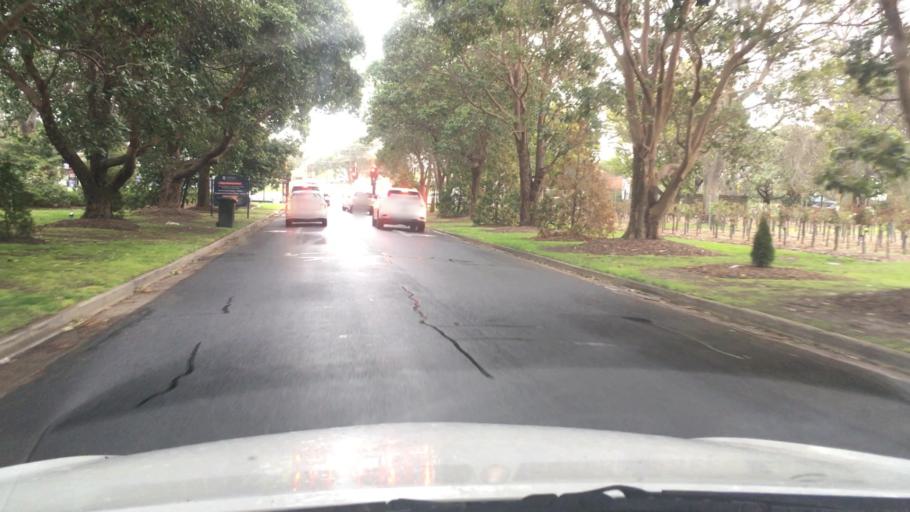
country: AU
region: Victoria
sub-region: Greater Dandenong
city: Noble Park North
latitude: -37.9469
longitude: 145.1737
